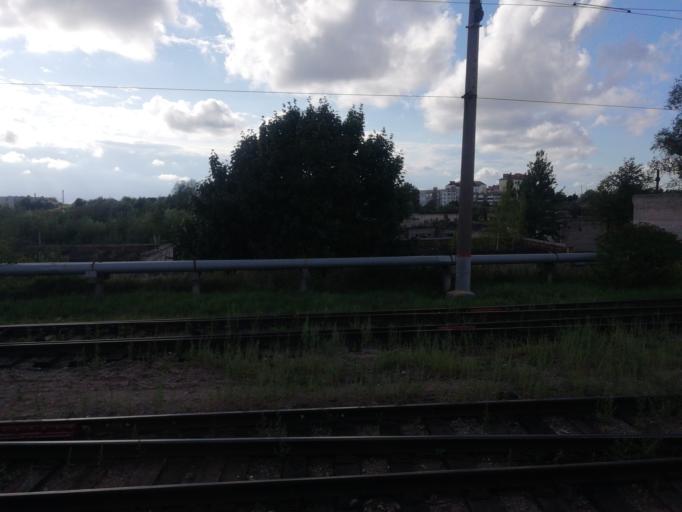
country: RU
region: Kaliningrad
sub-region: Gorod Kaliningrad
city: Kaliningrad
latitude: 54.6888
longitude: 20.4789
